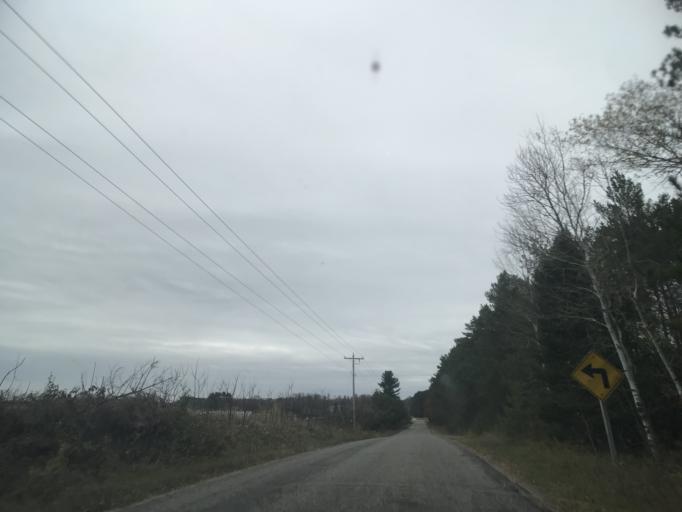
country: US
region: Wisconsin
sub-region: Menominee County
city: Legend Lake
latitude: 45.1788
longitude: -88.4552
